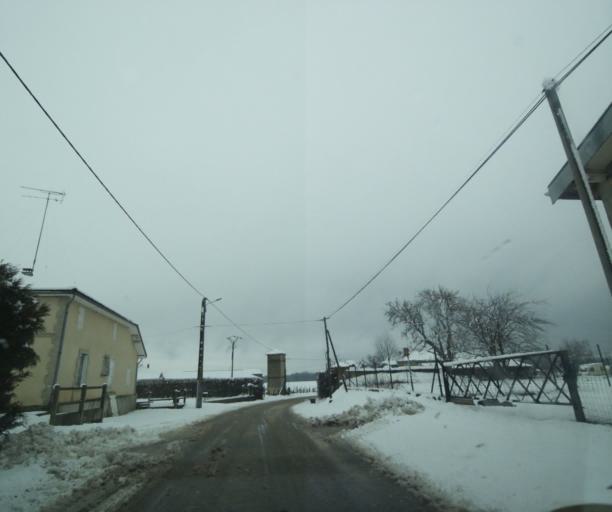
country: FR
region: Champagne-Ardenne
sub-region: Departement de la Haute-Marne
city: Montier-en-Der
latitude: 48.5102
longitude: 4.7804
